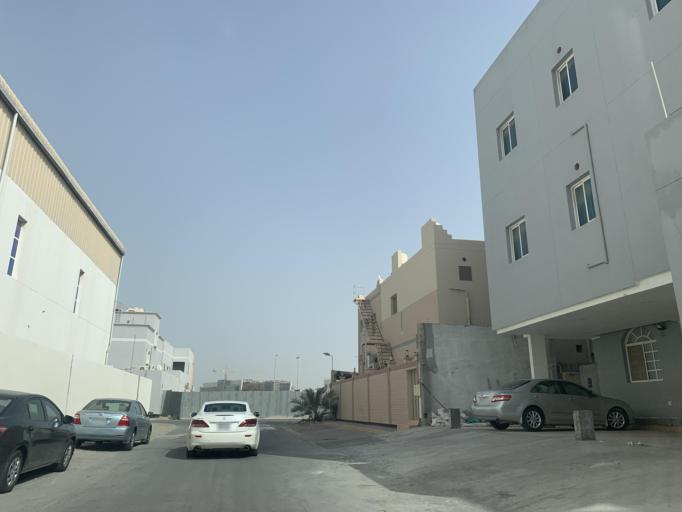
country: BH
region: Northern
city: Madinat `Isa
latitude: 26.1611
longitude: 50.5205
